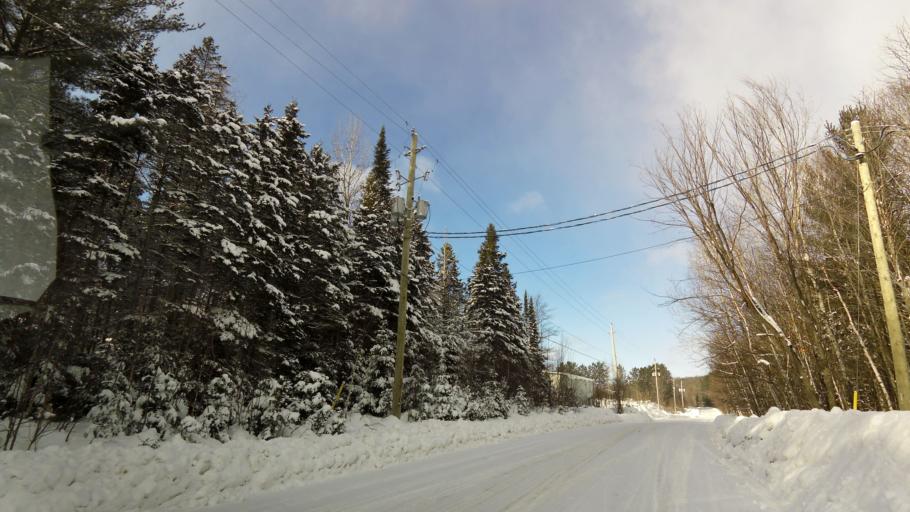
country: CA
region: Ontario
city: Bancroft
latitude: 45.0504
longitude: -78.5422
